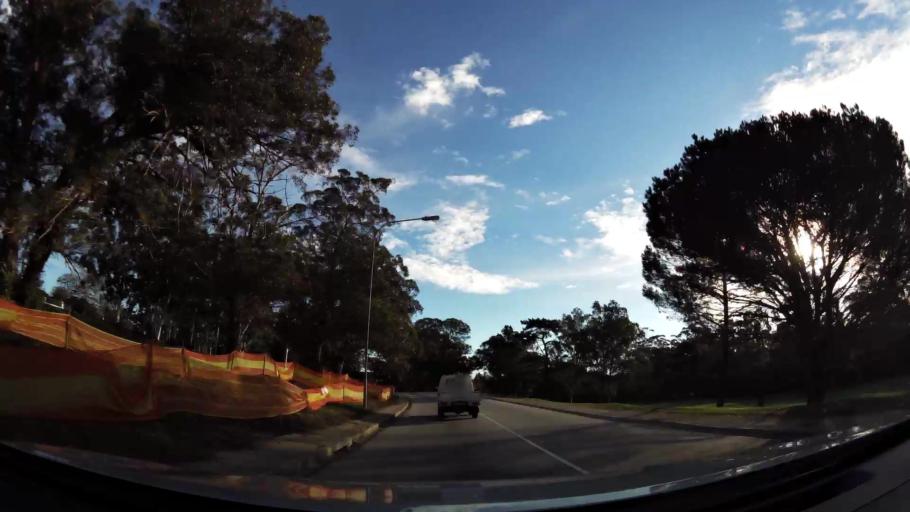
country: ZA
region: Eastern Cape
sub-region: Nelson Mandela Bay Metropolitan Municipality
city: Port Elizabeth
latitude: -33.9609
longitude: 25.5092
